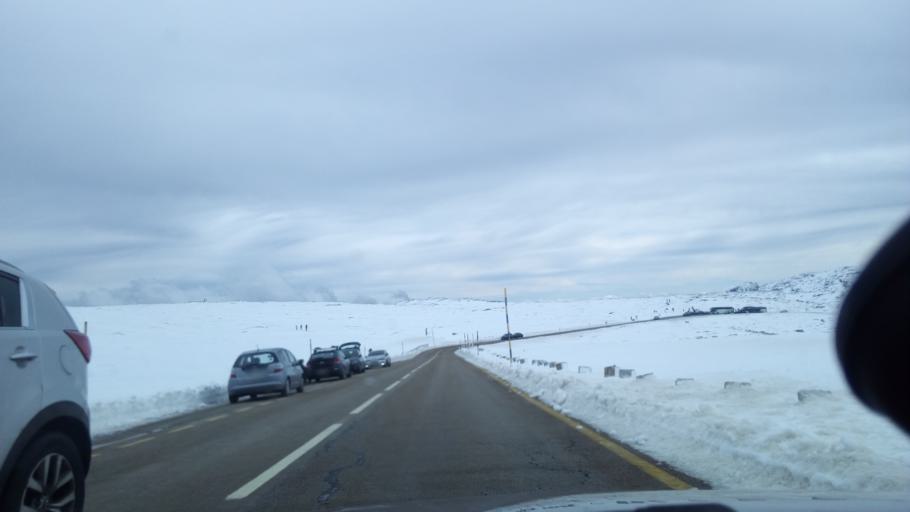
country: PT
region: Guarda
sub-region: Manteigas
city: Manteigas
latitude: 40.3416
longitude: -7.6239
